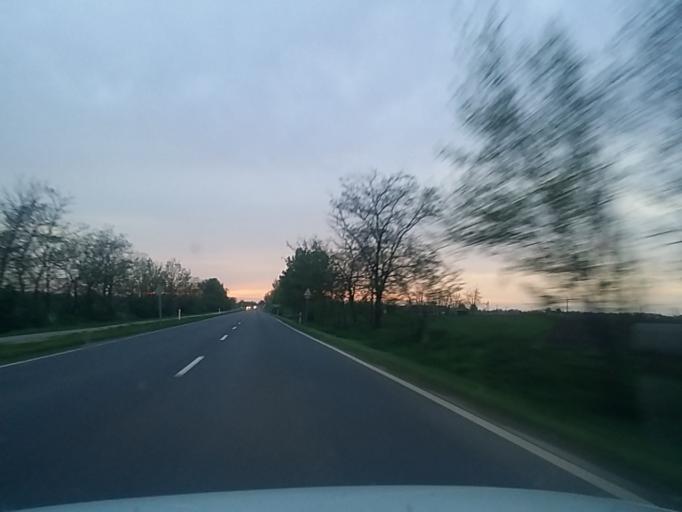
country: HU
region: Bekes
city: Kondoros
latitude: 46.7274
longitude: 20.9175
